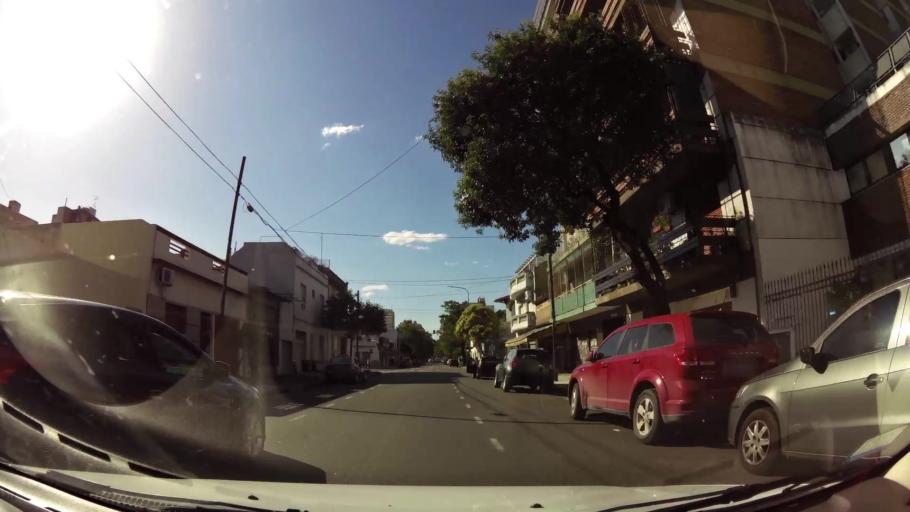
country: AR
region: Buenos Aires F.D.
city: Villa Santa Rita
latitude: -34.6139
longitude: -58.4659
